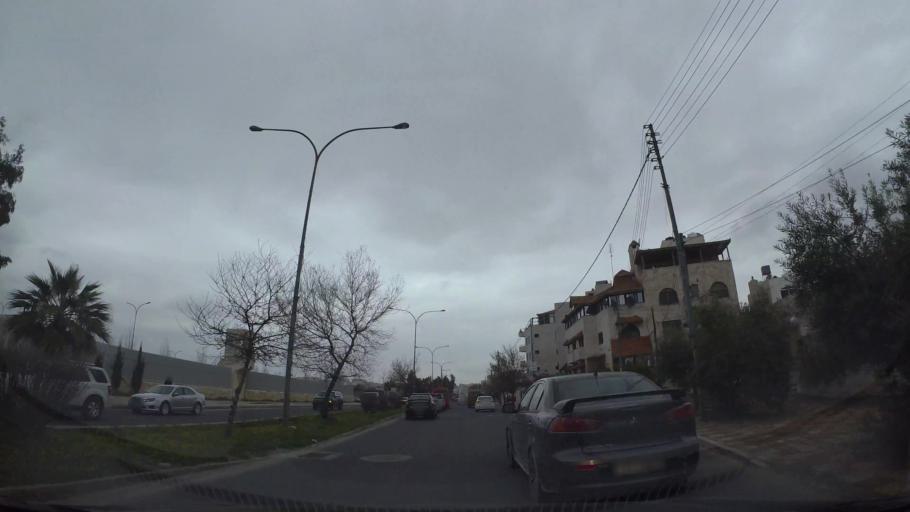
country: JO
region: Amman
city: Wadi as Sir
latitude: 31.9691
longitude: 35.8354
